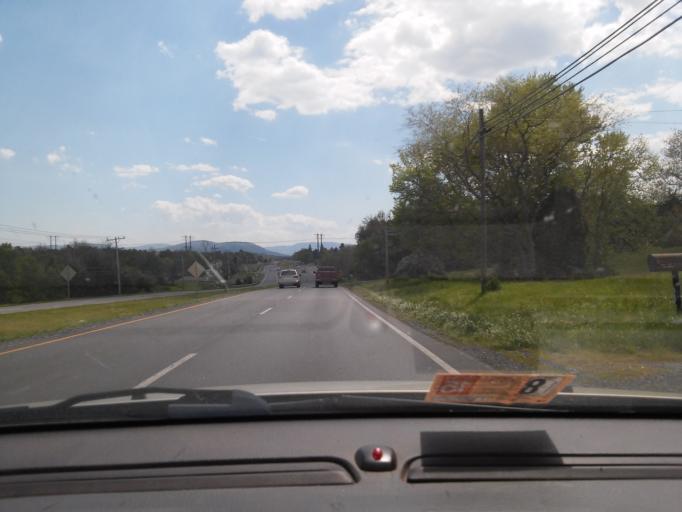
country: US
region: Virginia
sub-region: Warren County
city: Front Royal
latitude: 38.9815
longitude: -78.1834
